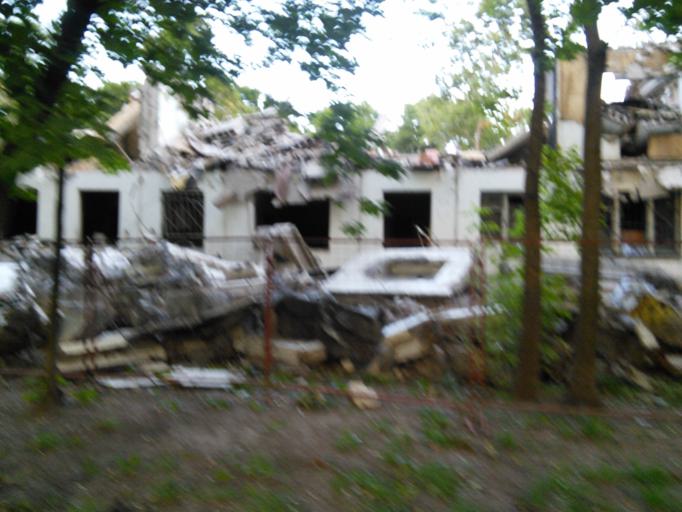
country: RU
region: Moscow
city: Novyye Kuz'minki
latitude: 55.7086
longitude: 37.7534
